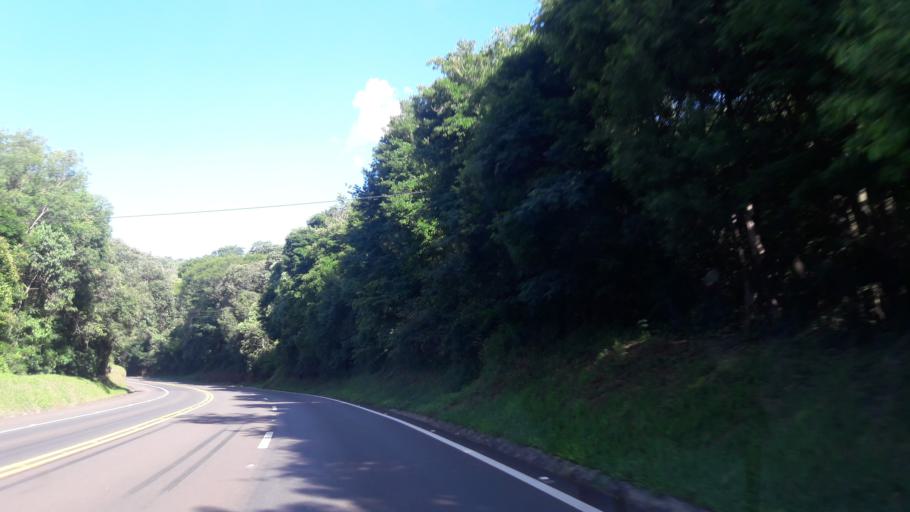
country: BR
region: Parana
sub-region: Laranjeiras Do Sul
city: Laranjeiras do Sul
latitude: -25.4189
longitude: -52.0547
